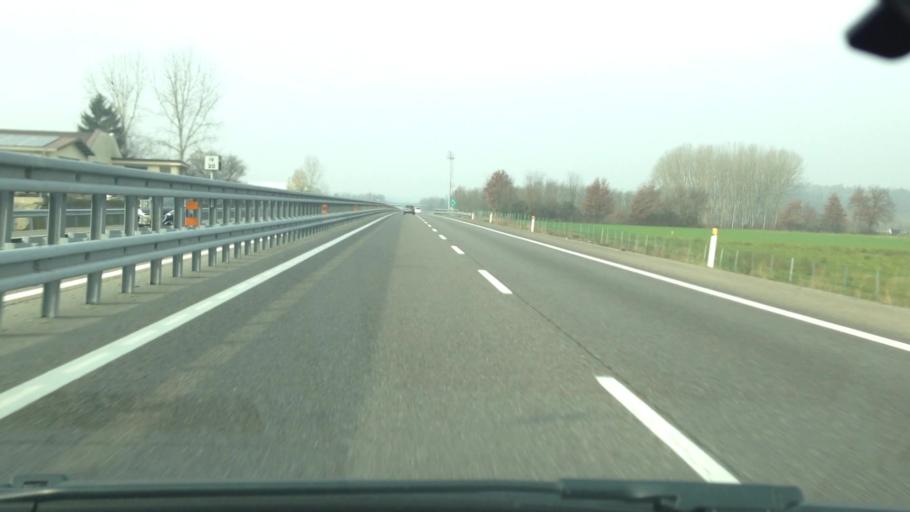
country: IT
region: Piedmont
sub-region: Provincia di Asti
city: Villafranca d'Asti
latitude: 44.9180
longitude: 8.0306
